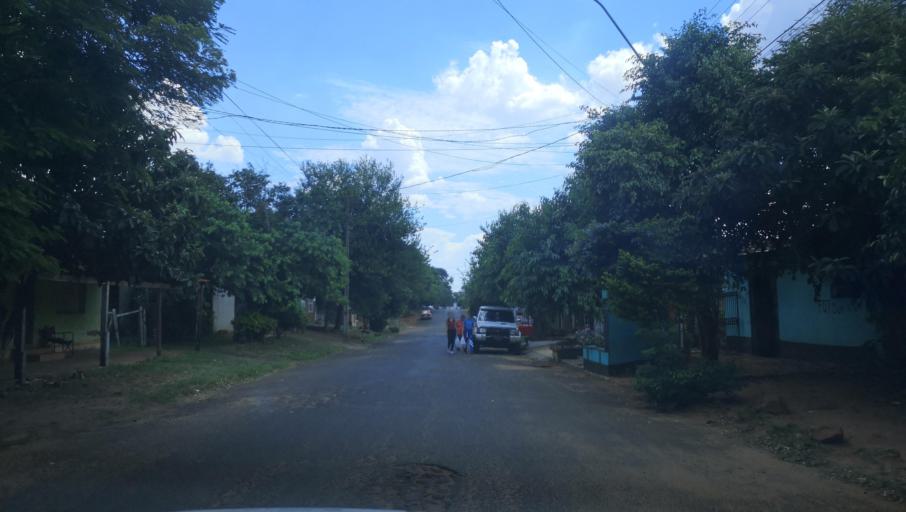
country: PY
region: Misiones
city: Santa Maria
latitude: -26.8906
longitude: -57.0285
